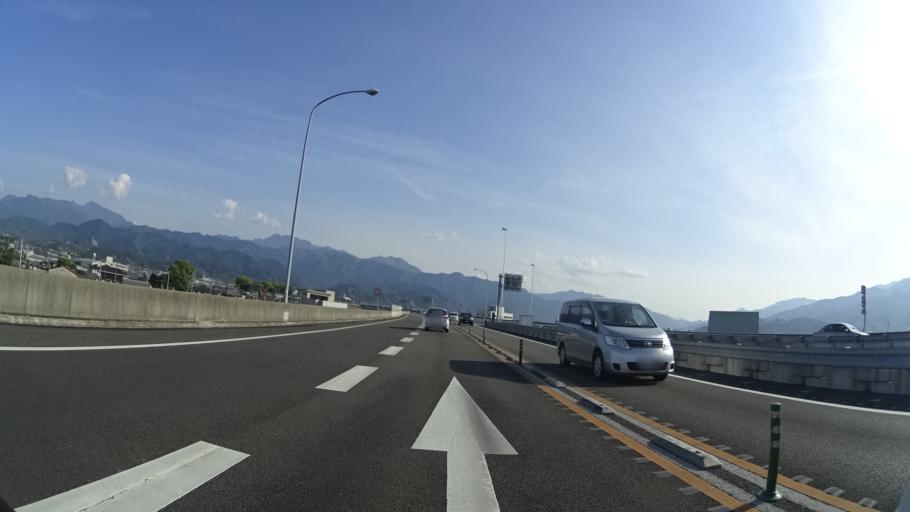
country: JP
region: Ehime
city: Saijo
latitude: 33.9161
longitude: 133.0730
